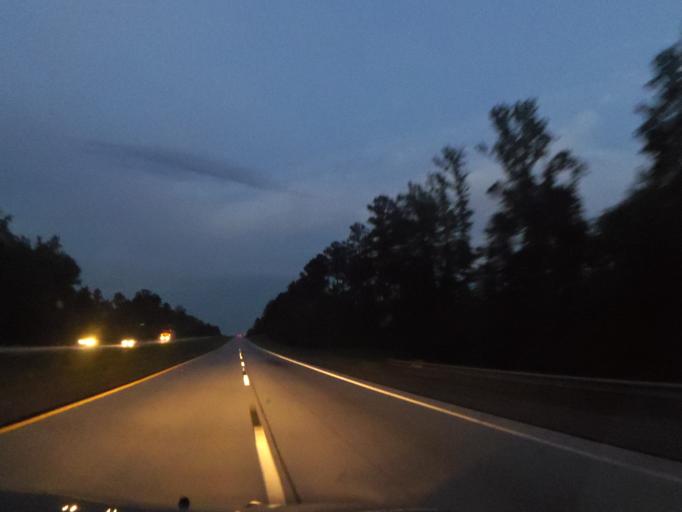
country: US
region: Georgia
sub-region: McDuffie County
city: Thomson
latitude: 33.5078
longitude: -82.4140
